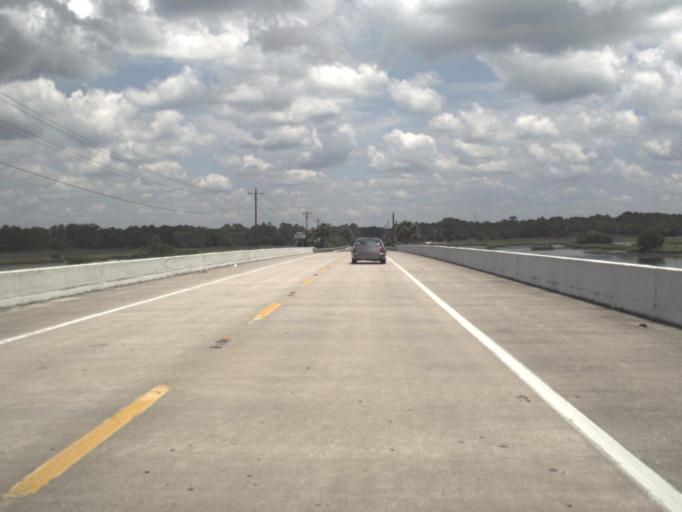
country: US
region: Florida
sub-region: Levy County
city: Chiefland
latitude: 29.1655
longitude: -83.0275
